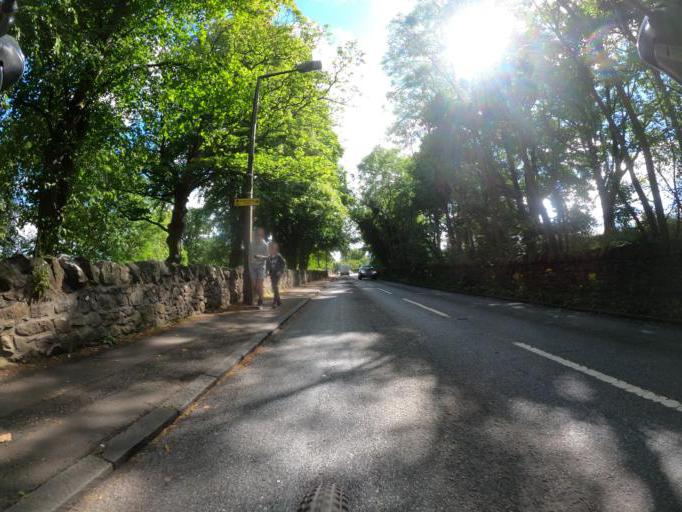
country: GB
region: Scotland
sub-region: Edinburgh
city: Colinton
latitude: 55.9503
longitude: -3.2524
